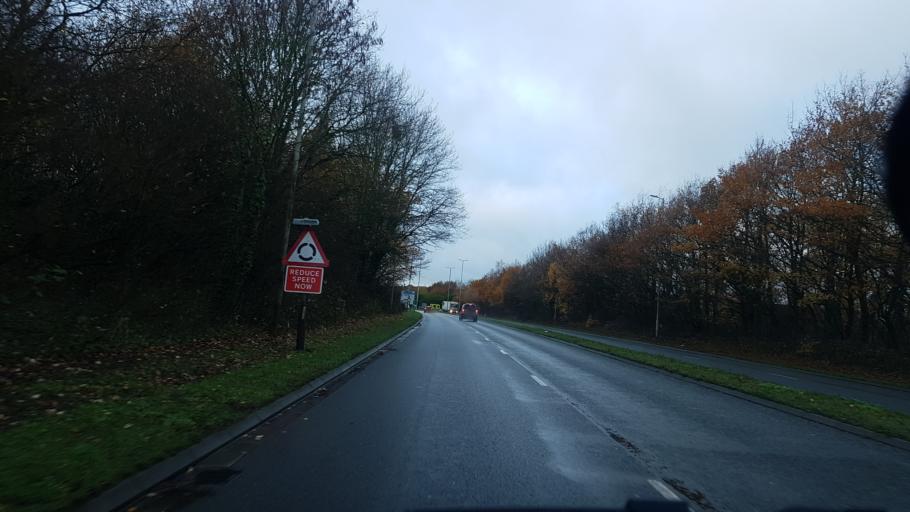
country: GB
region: England
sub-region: Bracknell Forest
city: Bracknell
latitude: 51.4135
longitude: -0.7713
